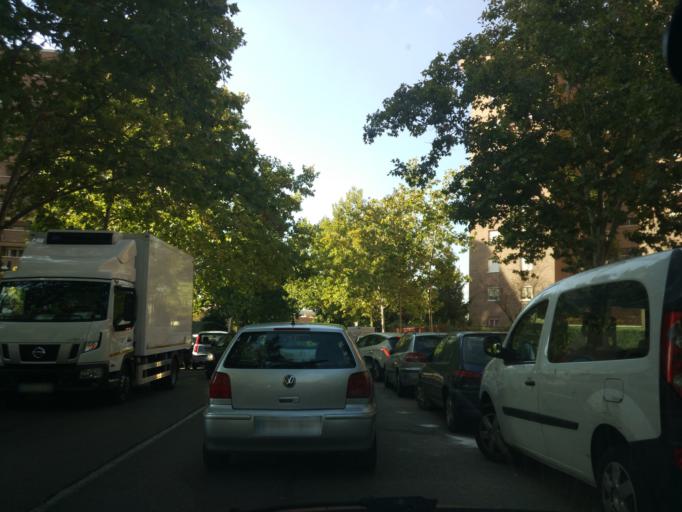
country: ES
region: Madrid
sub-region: Provincia de Madrid
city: Tetuan de las Victorias
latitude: 40.4734
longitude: -3.7188
